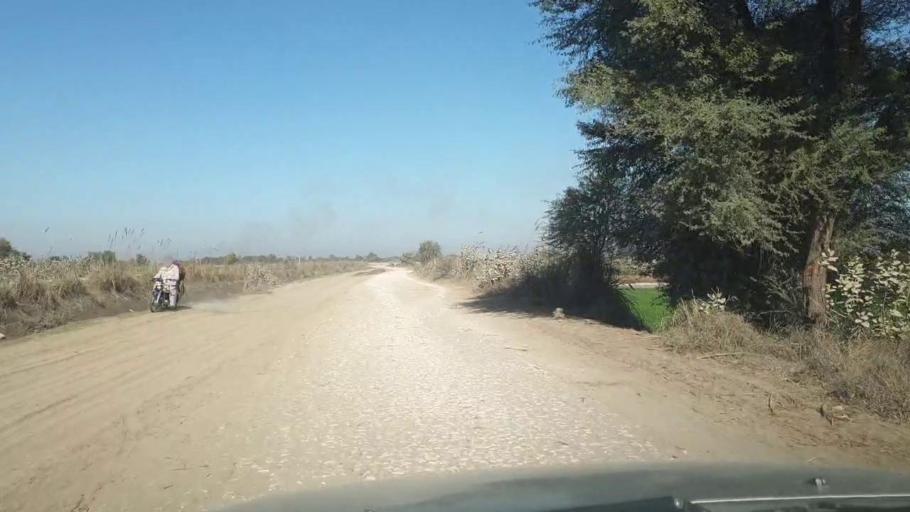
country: PK
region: Sindh
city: Ghotki
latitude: 28.0792
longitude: 69.3455
